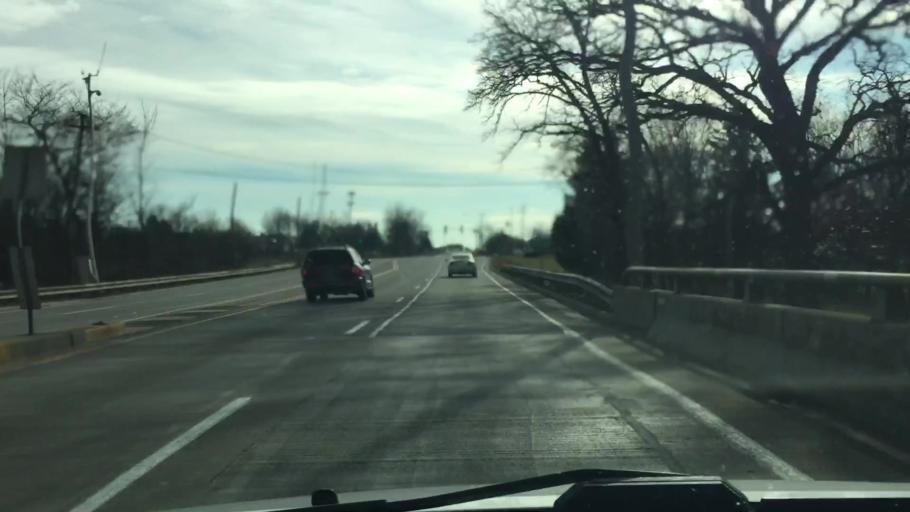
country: US
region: Illinois
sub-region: Kane County
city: Geneva
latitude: 41.8807
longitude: -88.2782
